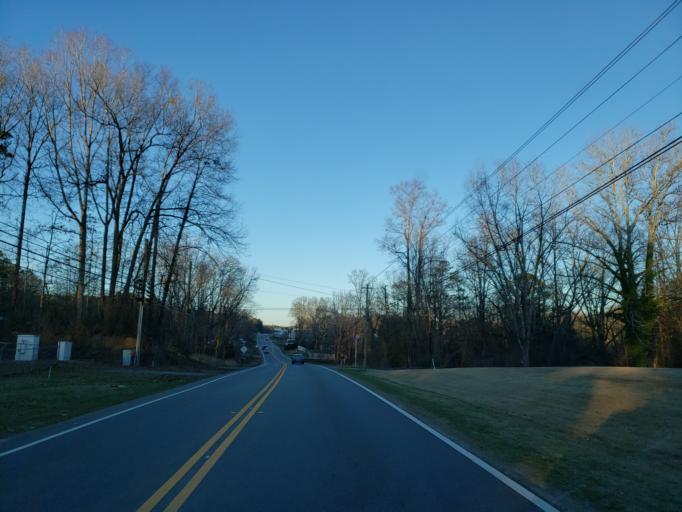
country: US
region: Georgia
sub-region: Cherokee County
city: Canton
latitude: 34.2699
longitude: -84.4560
